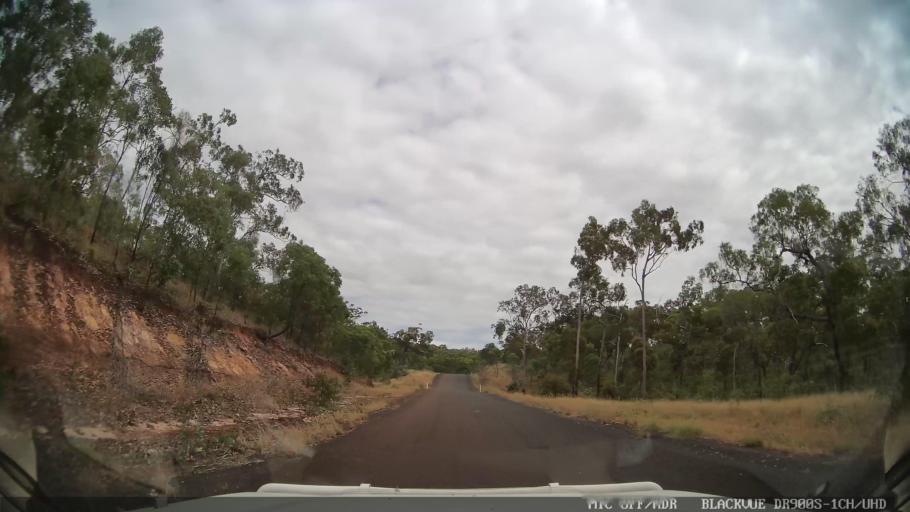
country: AU
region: Queensland
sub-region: Cook
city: Cooktown
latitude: -15.2822
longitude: 144.9112
